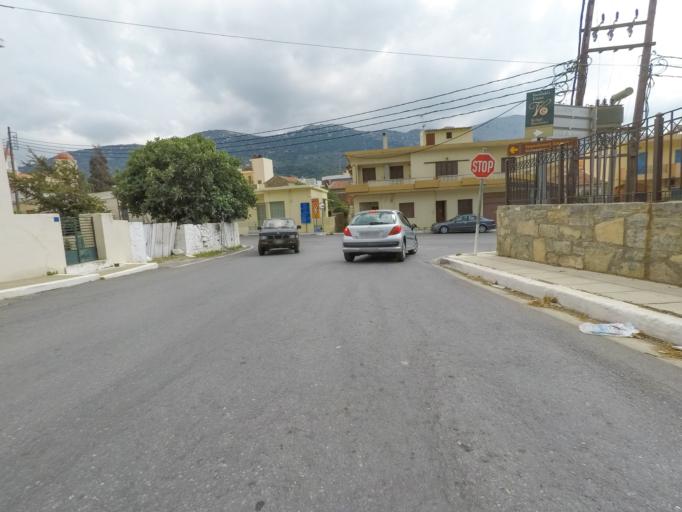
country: GR
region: Crete
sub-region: Nomos Lasithiou
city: Neapoli
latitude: 35.2583
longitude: 25.6077
